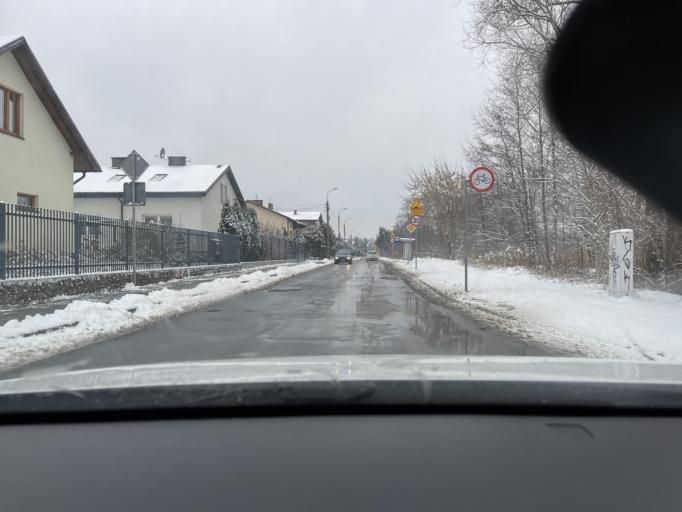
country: PL
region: Masovian Voivodeship
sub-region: Powiat zyrardowski
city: Zyrardow
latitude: 52.0429
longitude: 20.4458
